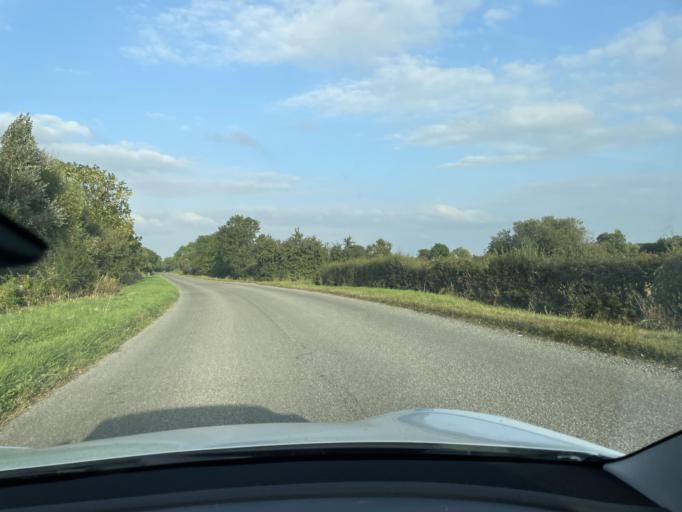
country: GB
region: England
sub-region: Bedford
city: Swineshead
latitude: 52.3650
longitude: -0.4313
